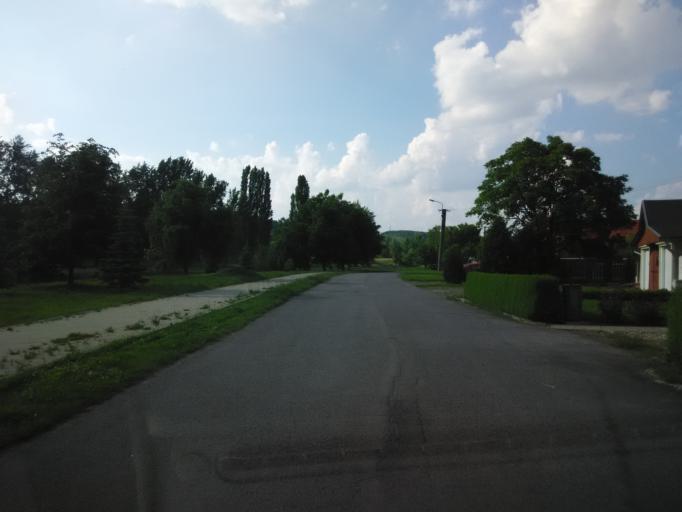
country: SK
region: Nitriansky
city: Tlmace
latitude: 48.2917
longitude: 18.5317
